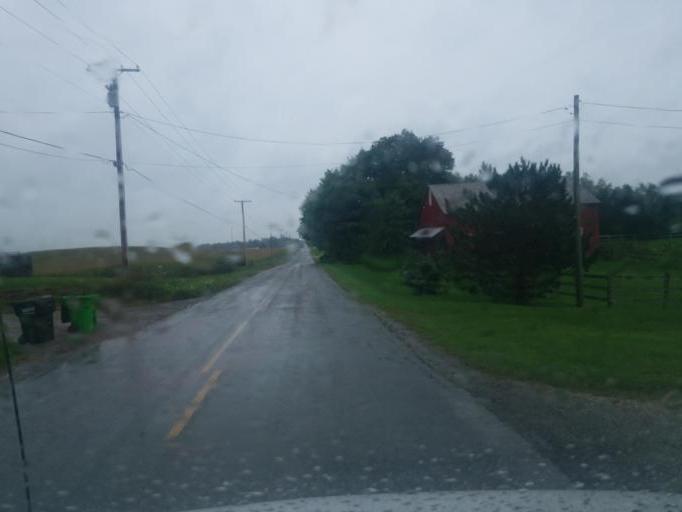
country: US
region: Ohio
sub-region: Medina County
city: Seville
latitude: 41.0437
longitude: -81.8322
